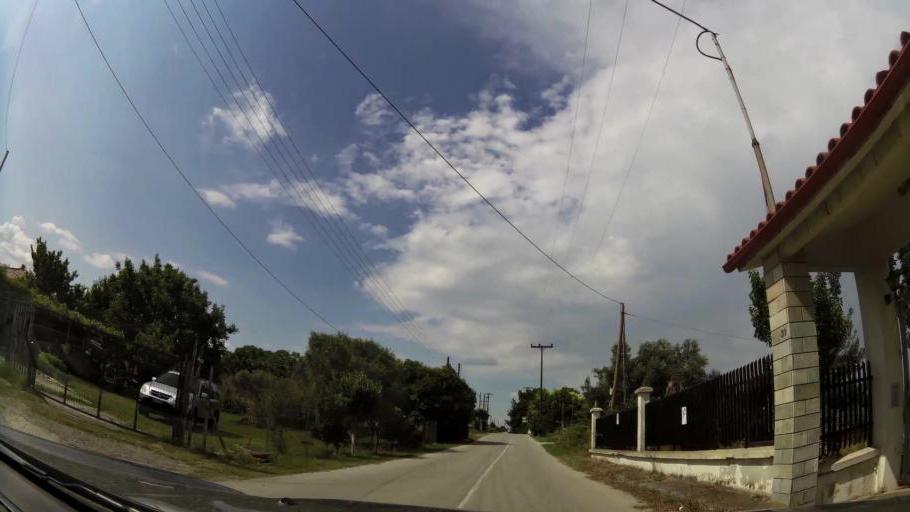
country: GR
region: Central Macedonia
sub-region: Nomos Pierias
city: Makrygialos
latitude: 40.3952
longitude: 22.6165
